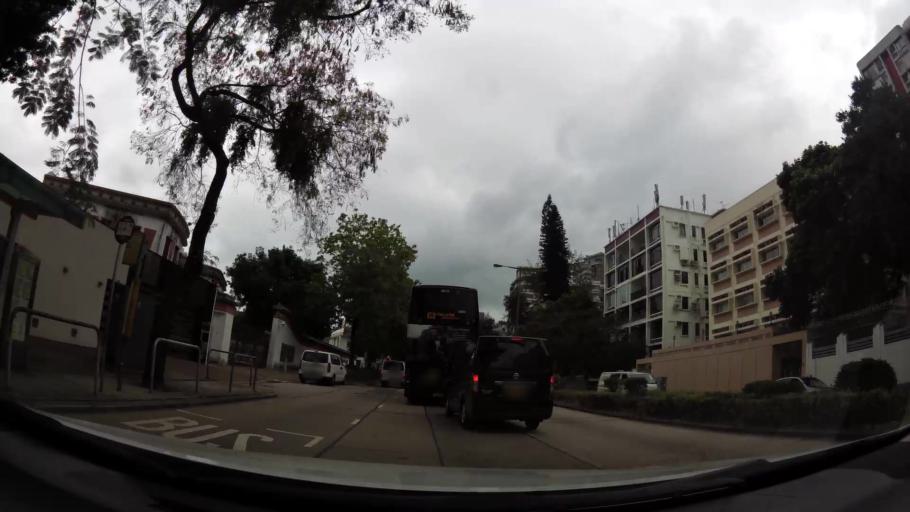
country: HK
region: Wong Tai Sin
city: Wong Tai Sin
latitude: 22.3401
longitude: 114.1767
